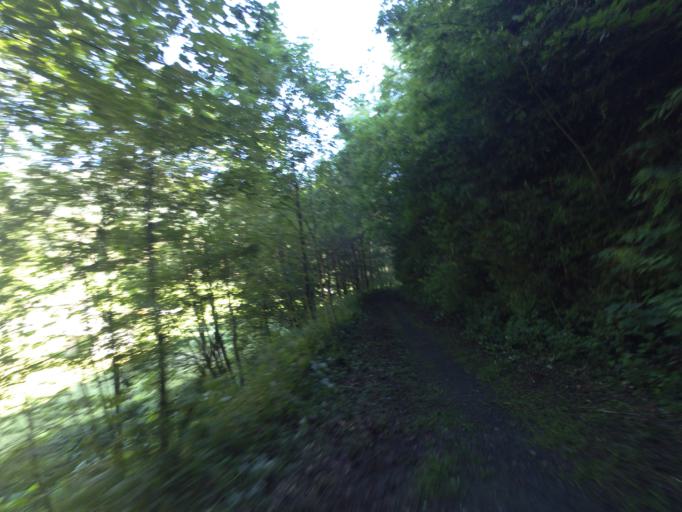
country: AT
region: Salzburg
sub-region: Politischer Bezirk Sankt Johann im Pongau
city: Goldegg
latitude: 47.3242
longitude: 13.0806
